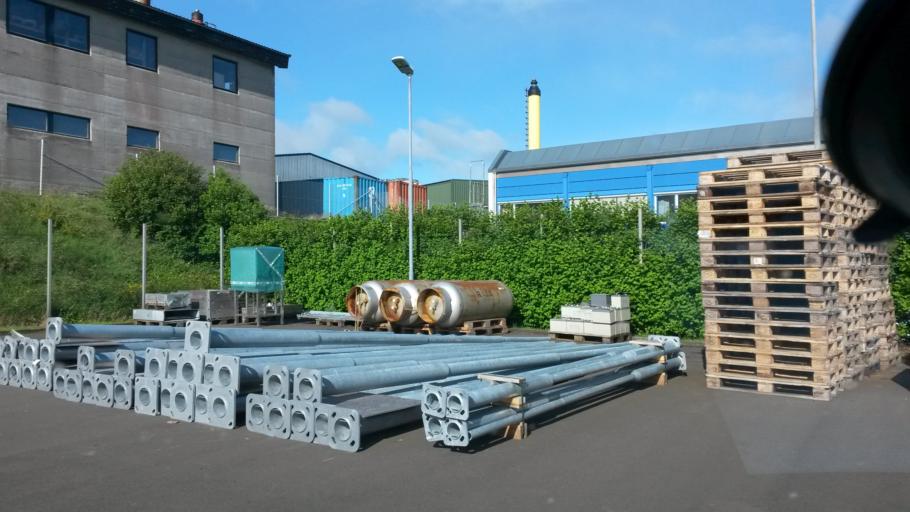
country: FO
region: Streymoy
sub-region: Torshavn
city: Torshavn
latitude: 62.0202
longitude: -6.7661
